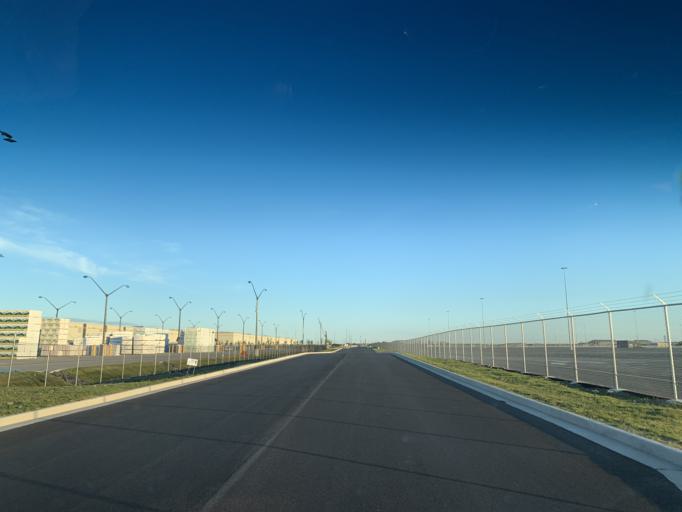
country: US
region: Maryland
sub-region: Baltimore County
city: Edgemere
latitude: 39.2236
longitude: -76.4858
